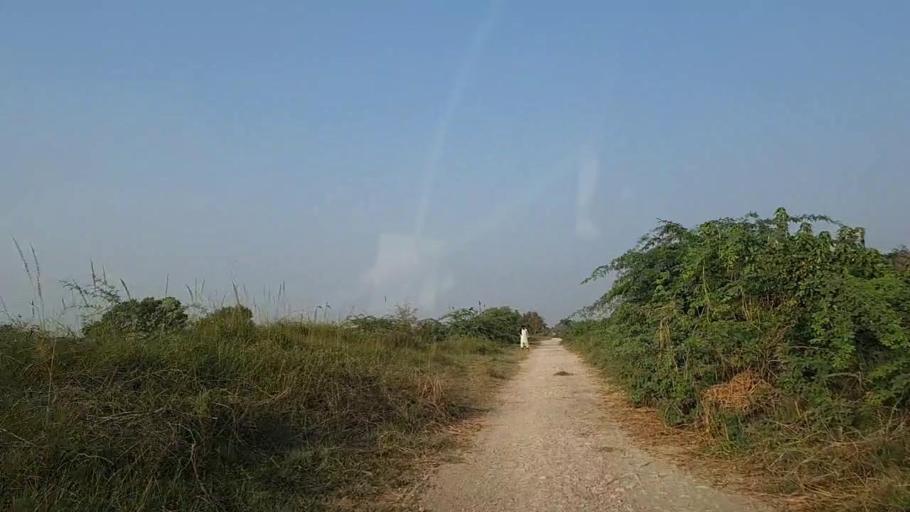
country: PK
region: Sindh
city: Thatta
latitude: 24.6688
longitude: 67.7813
